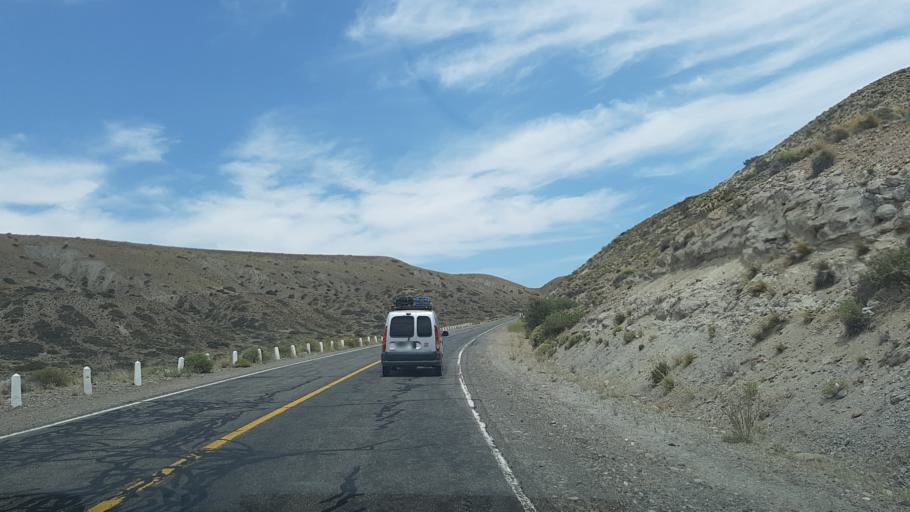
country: AR
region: Rio Negro
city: Pilcaniyeu
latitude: -40.4701
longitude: -70.6573
